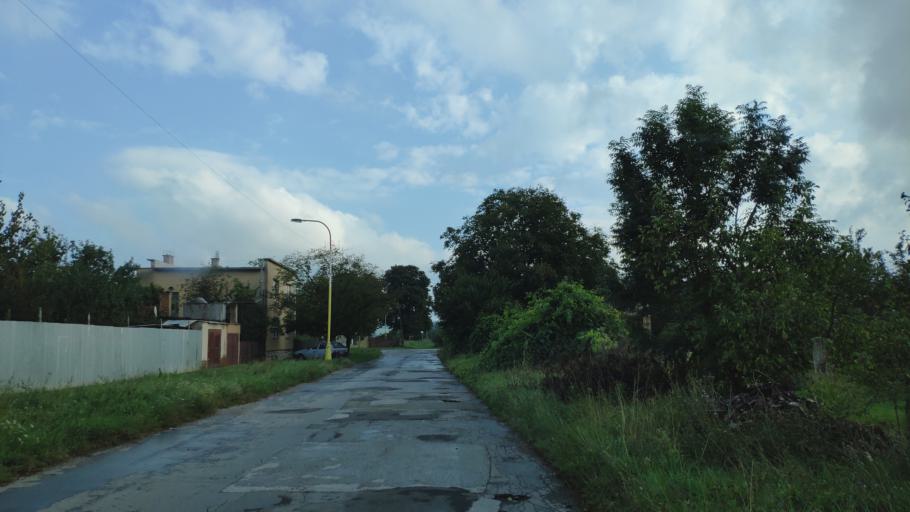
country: SK
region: Kosicky
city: Medzev
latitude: 48.5980
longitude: 20.8836
